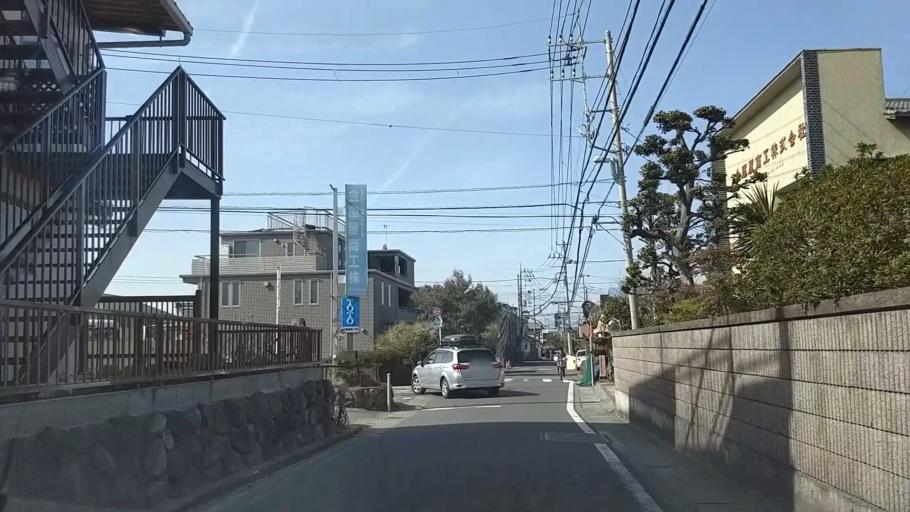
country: JP
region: Kanagawa
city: Chigasaki
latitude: 35.3465
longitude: 139.4240
